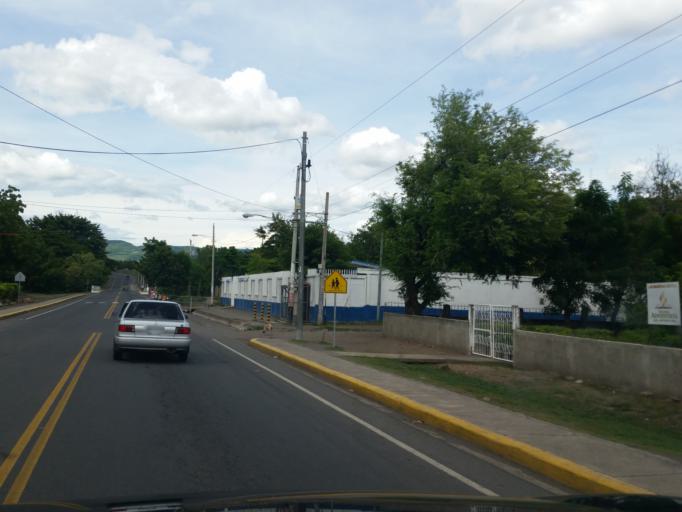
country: NI
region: Boaco
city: Teustepe
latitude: 12.4475
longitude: -86.0404
